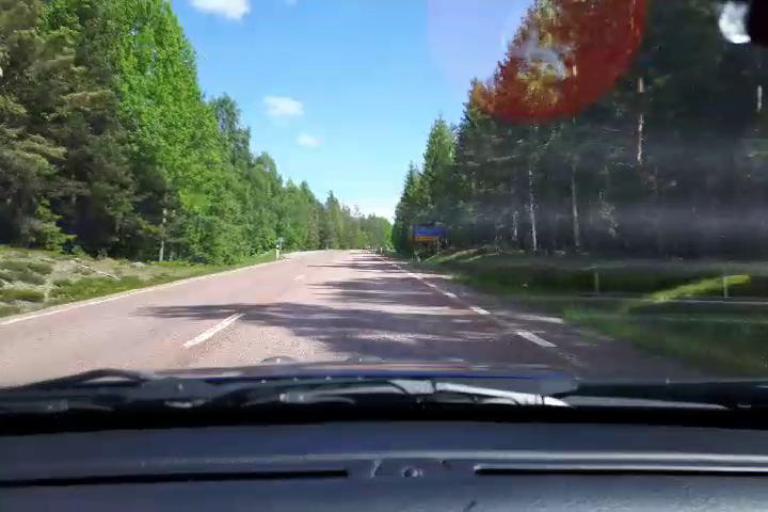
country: SE
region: Gaevleborg
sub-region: Hudiksvalls Kommun
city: Delsbo
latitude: 61.8049
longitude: 16.4573
